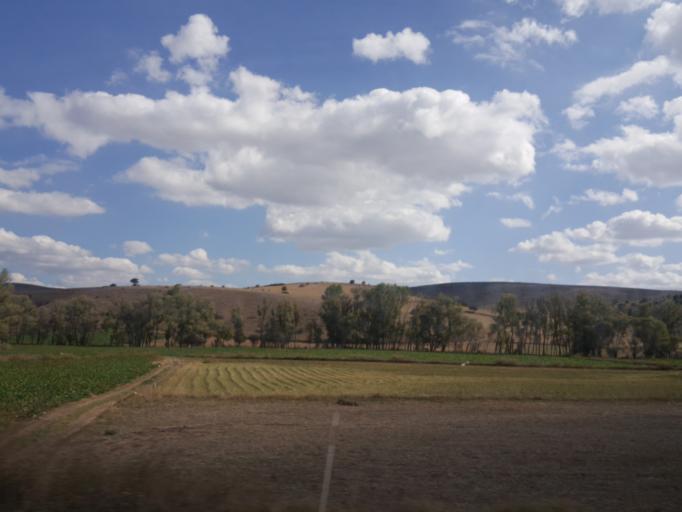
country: TR
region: Tokat
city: Camlibel
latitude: 40.1655
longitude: 36.4256
